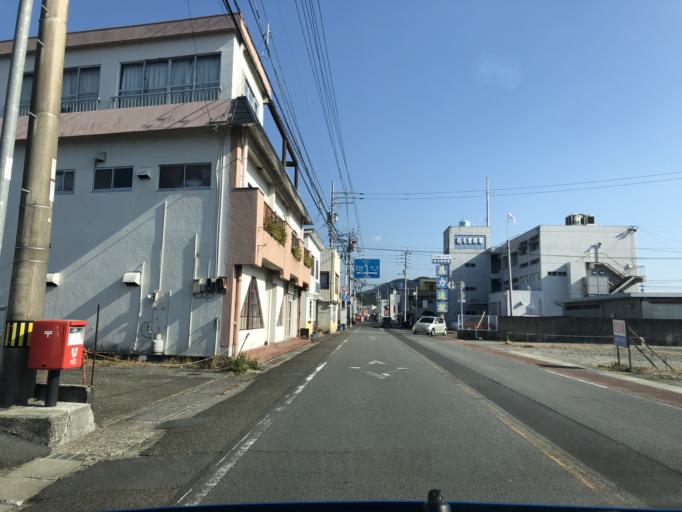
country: JP
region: Kochi
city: Sukumo
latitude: 32.9352
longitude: 132.7222
